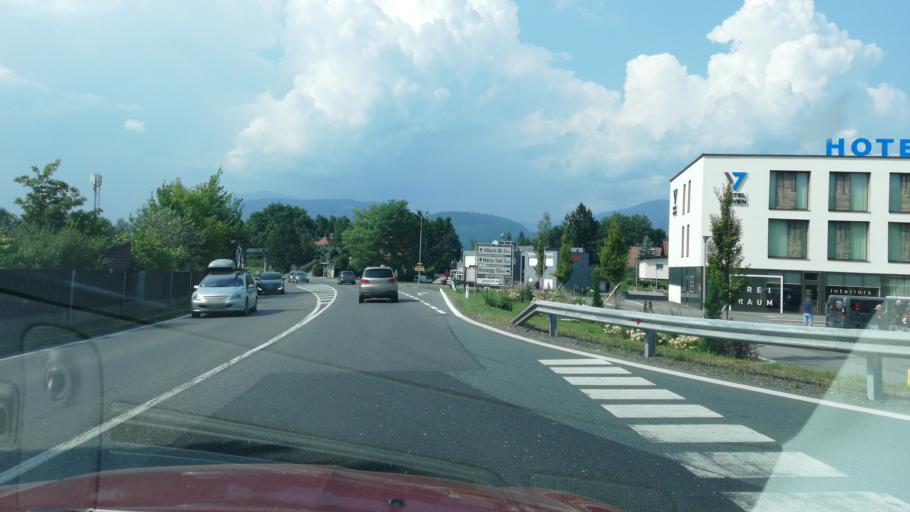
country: AT
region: Carinthia
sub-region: Villach Stadt
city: Villach
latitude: 46.6010
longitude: 13.8824
